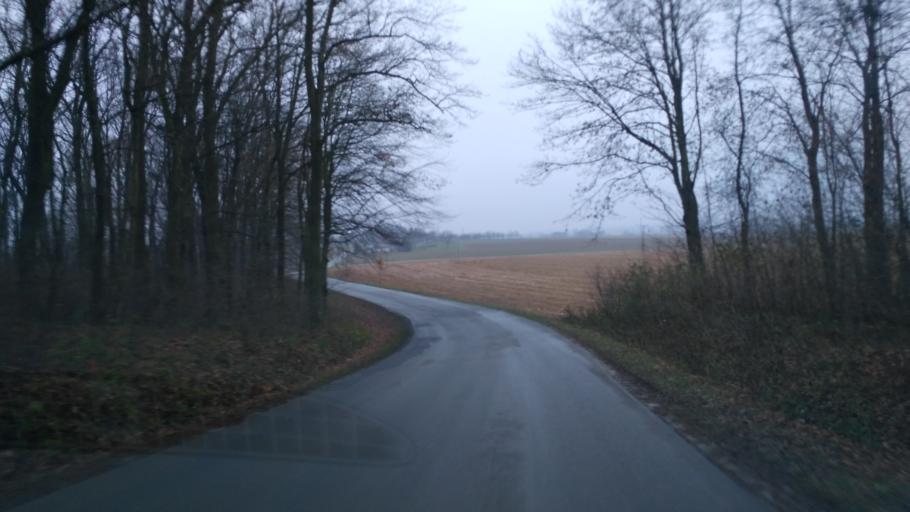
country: PL
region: Subcarpathian Voivodeship
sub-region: Powiat przeworski
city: Zurawiczki
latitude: 49.9996
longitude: 22.5052
